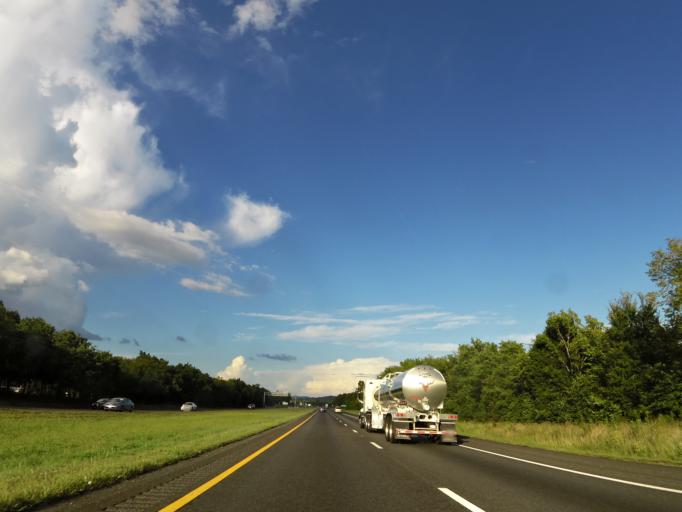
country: US
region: Tennessee
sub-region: Wilson County
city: Lebanon
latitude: 36.1906
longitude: -86.2583
